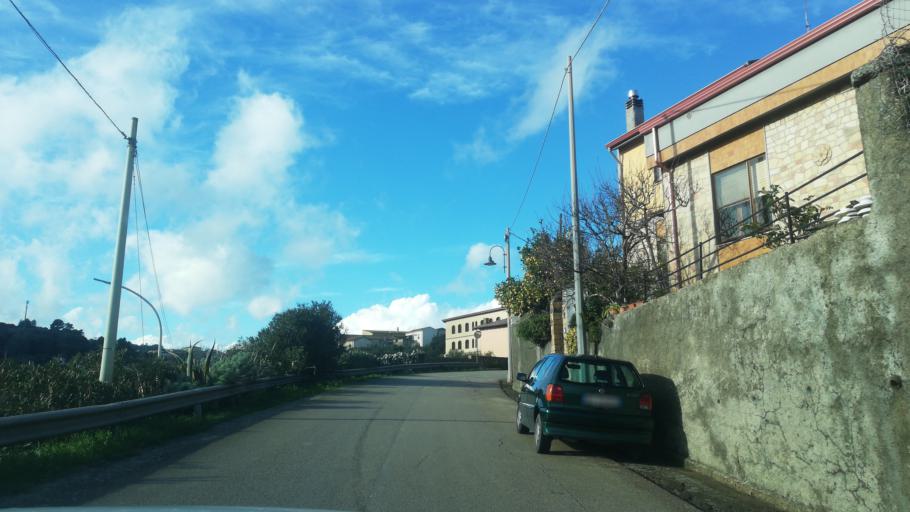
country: IT
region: Sardinia
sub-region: Provincia di Medio Campidano
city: Villanovaforru
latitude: 39.6302
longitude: 8.8733
